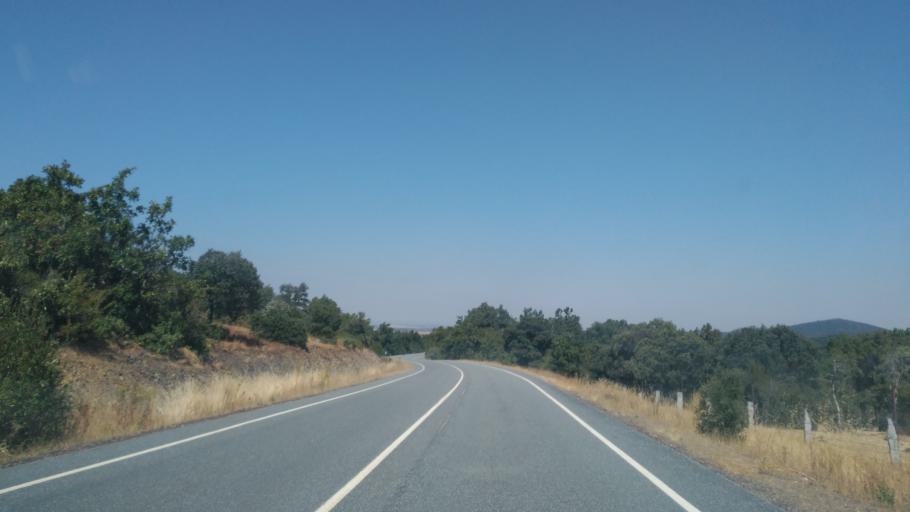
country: ES
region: Castille and Leon
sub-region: Provincia de Salamanca
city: Aldeanueva de la Sierra
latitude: 40.5959
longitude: -6.0916
